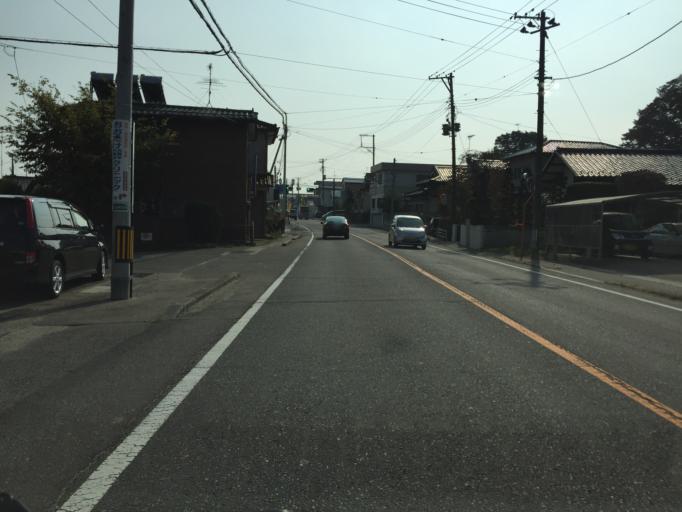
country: JP
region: Fukushima
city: Koriyama
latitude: 37.4284
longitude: 140.3924
